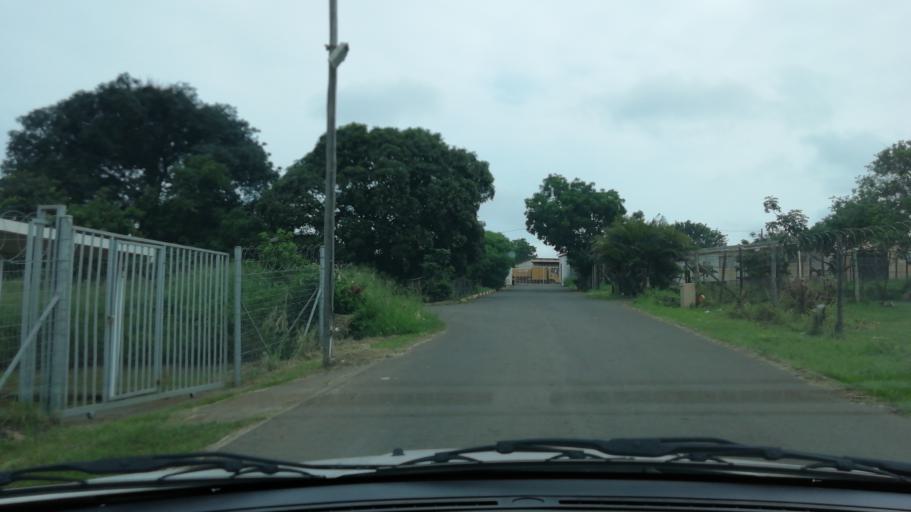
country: ZA
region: KwaZulu-Natal
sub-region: uThungulu District Municipality
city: Empangeni
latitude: -28.7404
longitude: 31.8842
